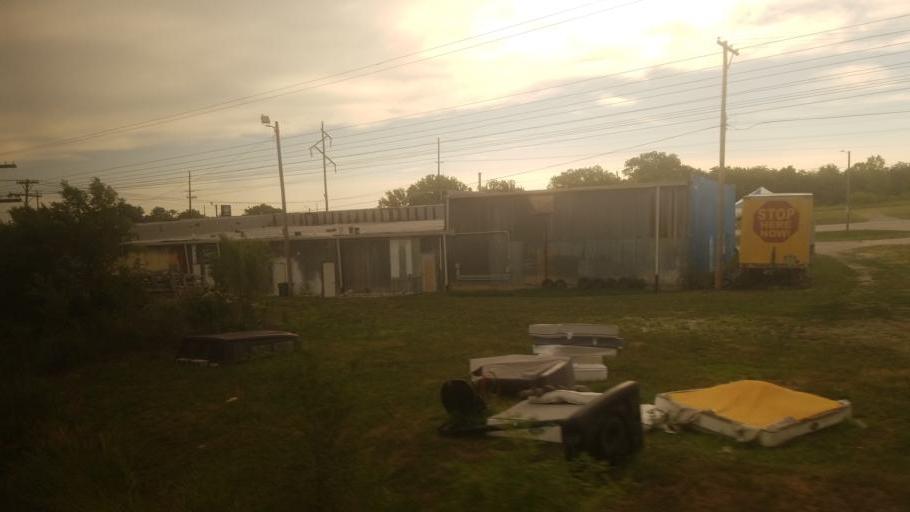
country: US
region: Kansas
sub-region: Shawnee County
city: Topeka
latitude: 38.9840
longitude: -95.6889
